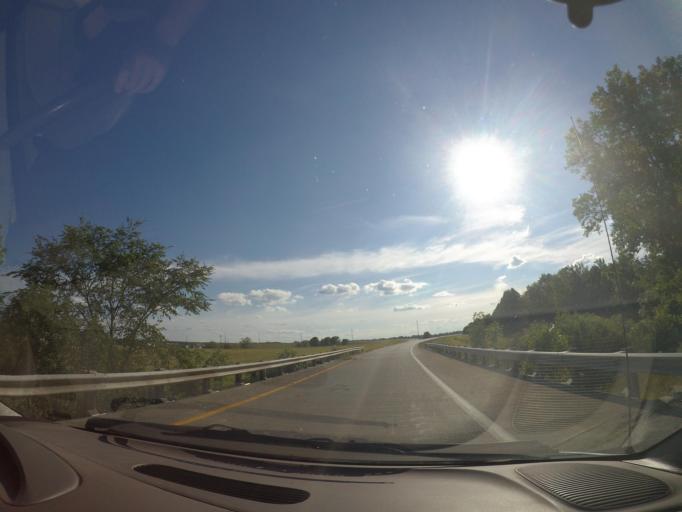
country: US
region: Ohio
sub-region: Henry County
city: Napoleon
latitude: 41.3989
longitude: -84.1460
